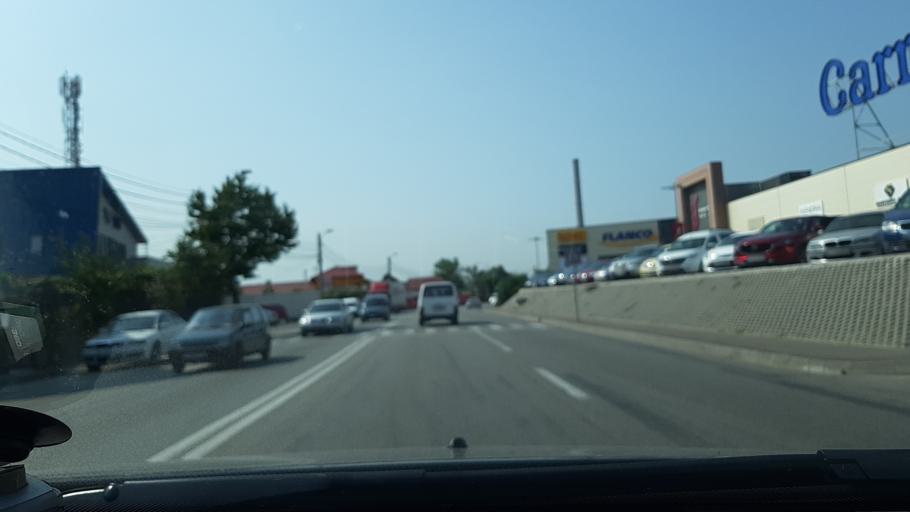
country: RO
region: Gorj
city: Targu Jiu
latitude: 45.0242
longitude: 23.2658
